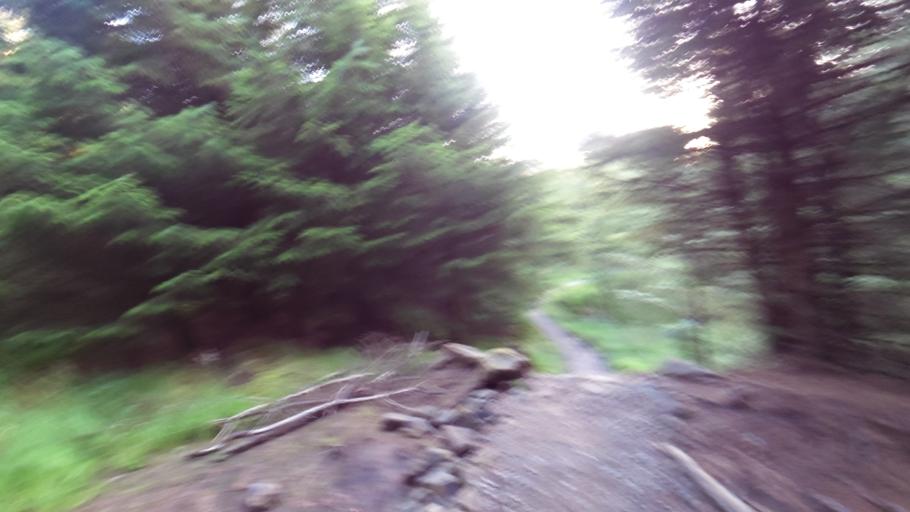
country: GB
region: England
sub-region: North Yorkshire
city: Settle
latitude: 54.0036
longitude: -2.3775
